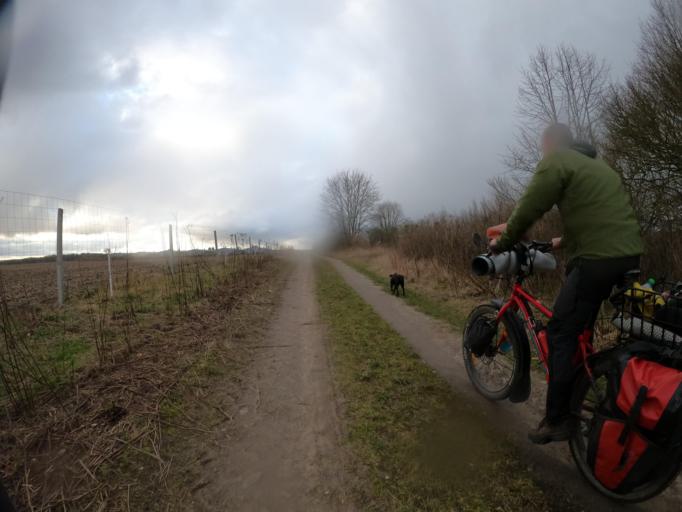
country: PL
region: Greater Poland Voivodeship
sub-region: Powiat zlotowski
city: Sypniewo
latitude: 53.4596
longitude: 16.5900
